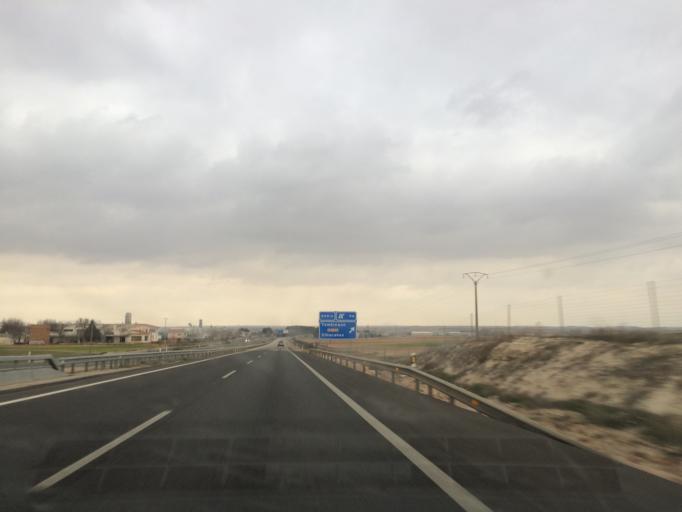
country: ES
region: Castille-La Mancha
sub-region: Province of Toledo
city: Tembleque
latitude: 39.6757
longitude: -3.5081
